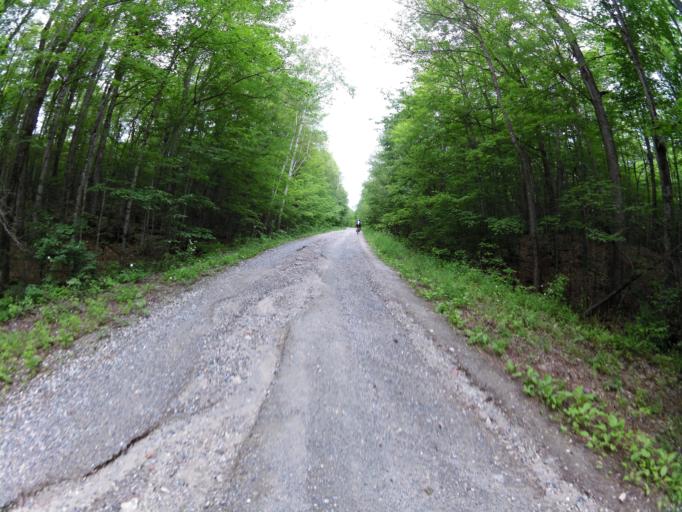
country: CA
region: Ontario
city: Perth
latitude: 45.0177
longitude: -76.5805
